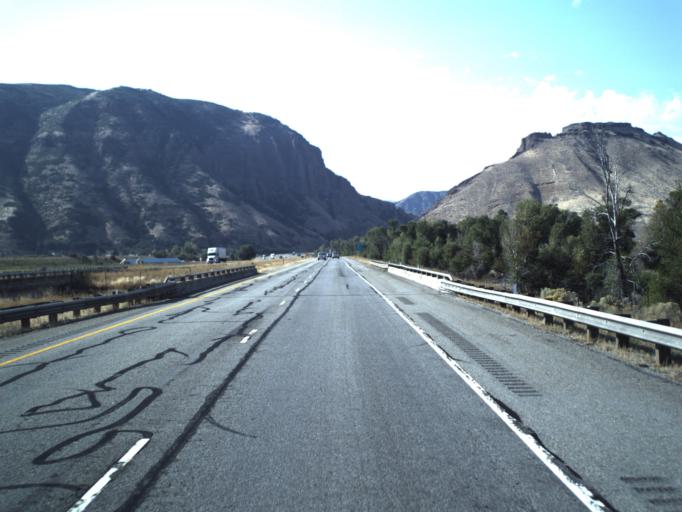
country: US
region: Utah
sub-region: Summit County
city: Coalville
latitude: 41.0355
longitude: -111.5093
